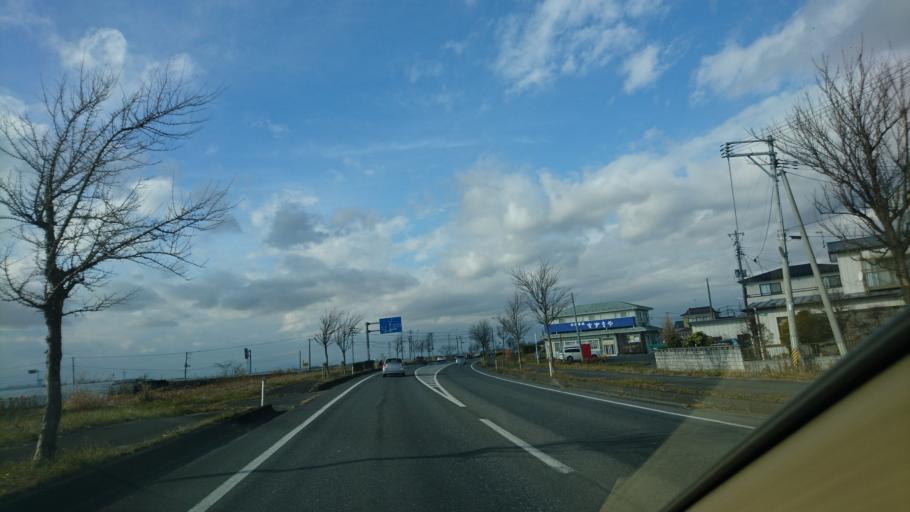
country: JP
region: Miyagi
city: Wakuya
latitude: 38.5330
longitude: 141.1236
